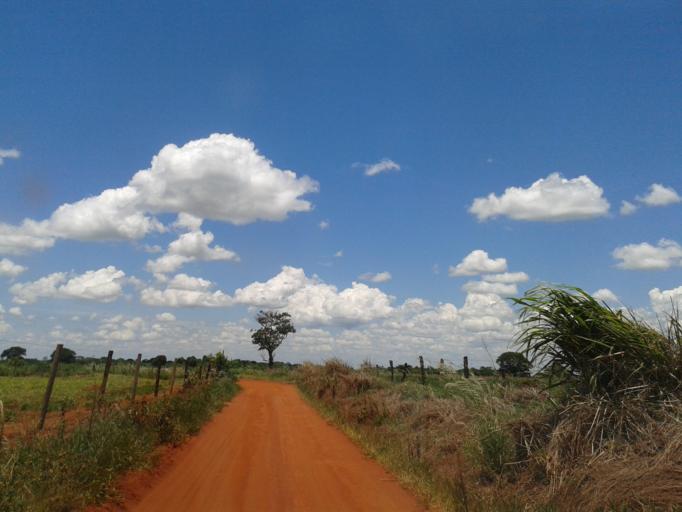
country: BR
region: Minas Gerais
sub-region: Centralina
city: Centralina
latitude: -18.6960
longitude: -49.1679
